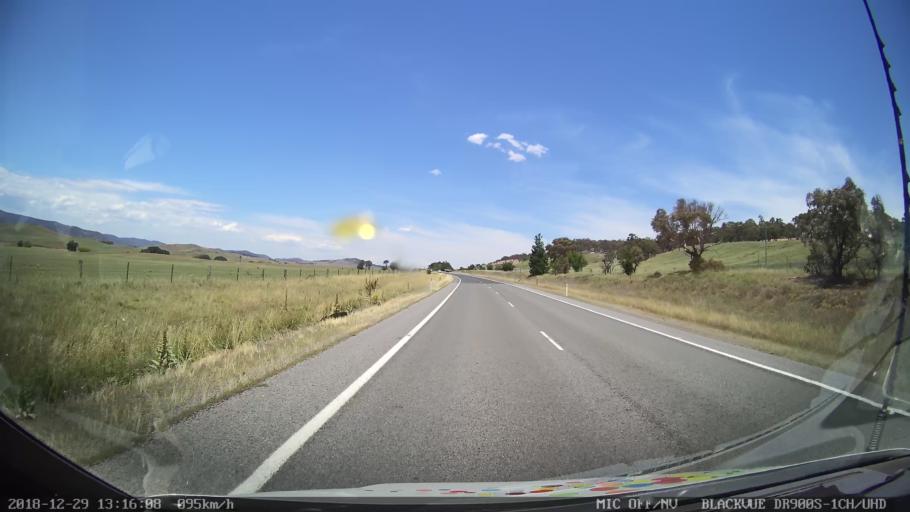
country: AU
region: Australian Capital Territory
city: Macarthur
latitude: -35.7189
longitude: 149.1584
